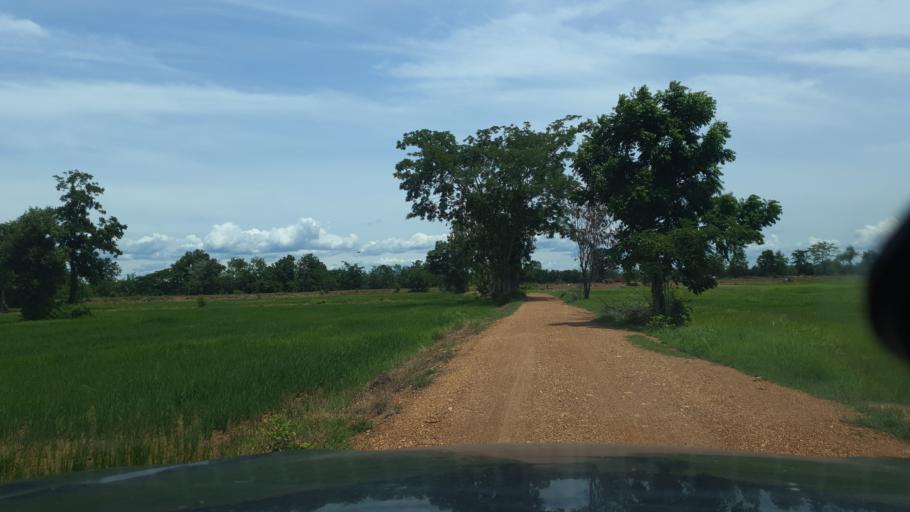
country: TH
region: Sukhothai
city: Ban Na
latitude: 17.0783
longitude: 99.6931
